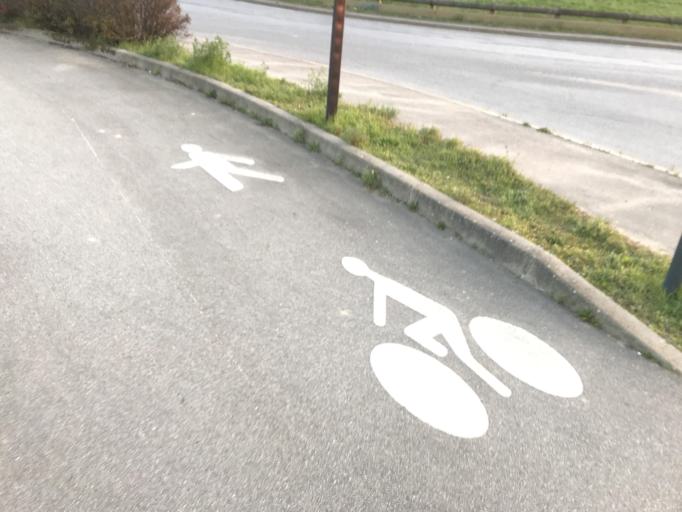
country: FR
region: Ile-de-France
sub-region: Departement de l'Essonne
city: Ballainvilliers
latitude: 48.6689
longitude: 2.2856
